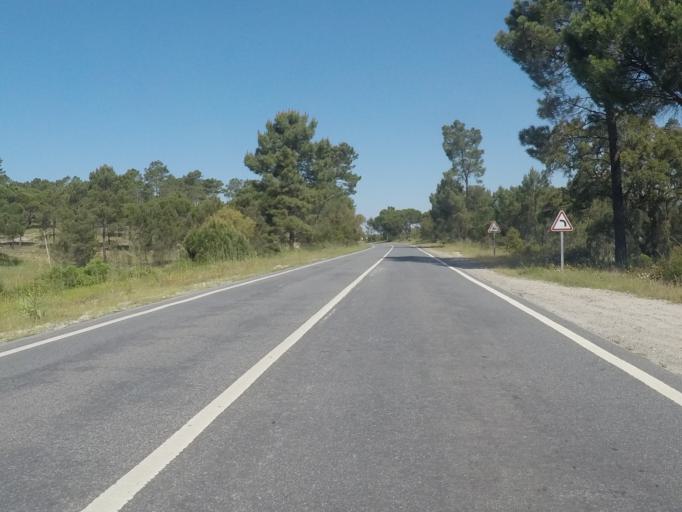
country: PT
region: Setubal
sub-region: Grandola
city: Grandola
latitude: 38.2975
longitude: -8.7250
